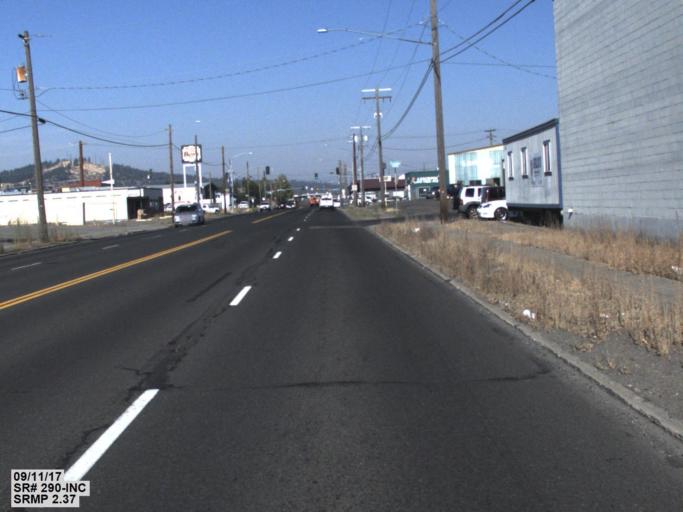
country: US
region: Washington
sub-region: Spokane County
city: Spokane
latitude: 47.6664
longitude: -117.3631
